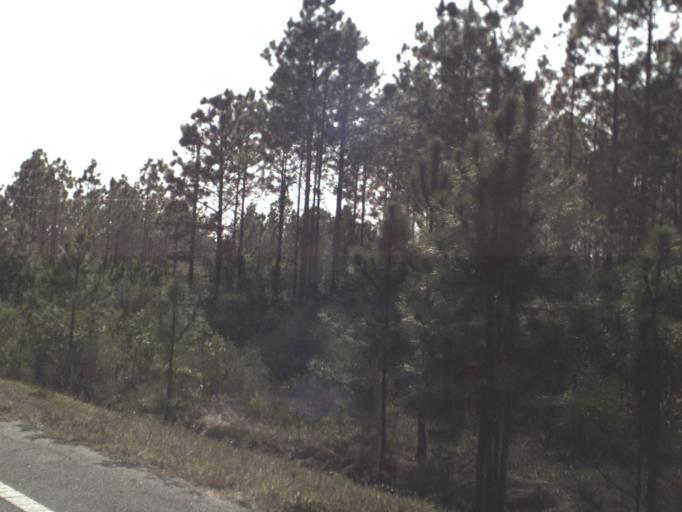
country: US
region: Florida
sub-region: Franklin County
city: Carrabelle
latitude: 29.9238
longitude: -84.5203
